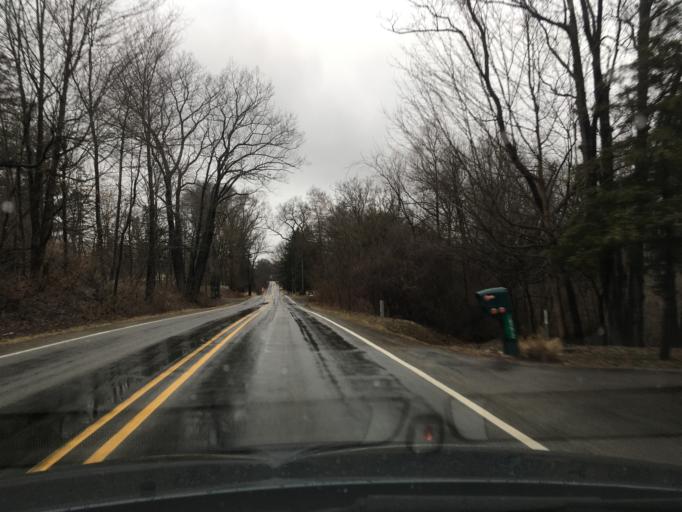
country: US
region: Michigan
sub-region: Washtenaw County
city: Chelsea
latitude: 42.3091
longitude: -84.0723
